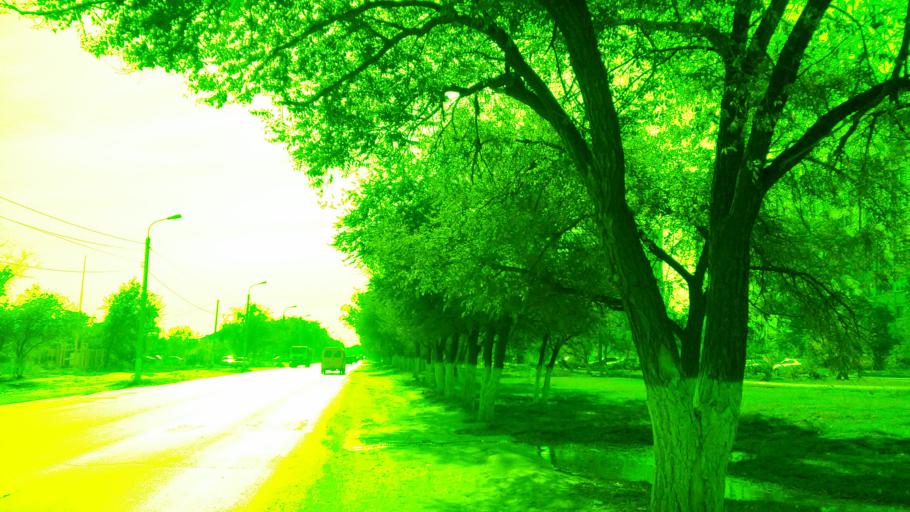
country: RU
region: Volgograd
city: Vodstroy
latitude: 48.8417
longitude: 44.6469
